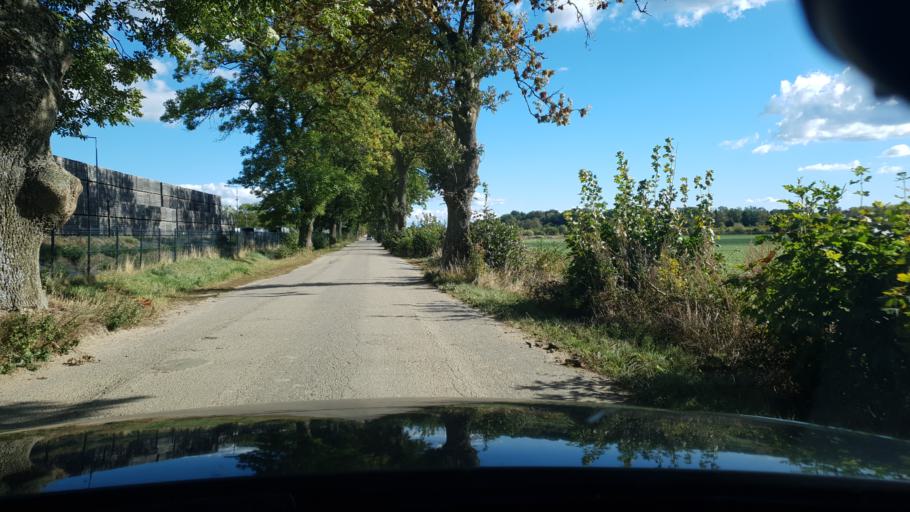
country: PL
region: Pomeranian Voivodeship
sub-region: Powiat pucki
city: Zelistrzewo
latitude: 54.6867
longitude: 18.4520
